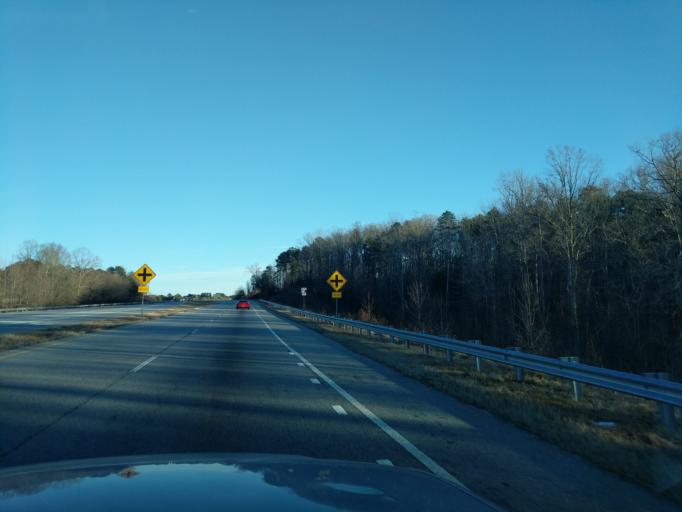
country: US
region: Georgia
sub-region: Stephens County
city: Toccoa
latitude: 34.5356
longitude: -83.3405
